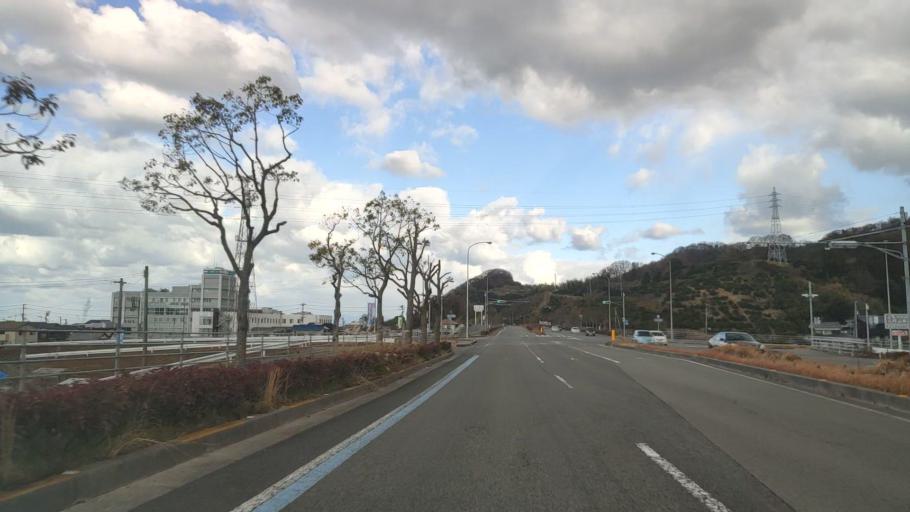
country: JP
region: Ehime
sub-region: Shikoku-chuo Shi
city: Matsuyama
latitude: 33.9021
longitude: 132.7569
